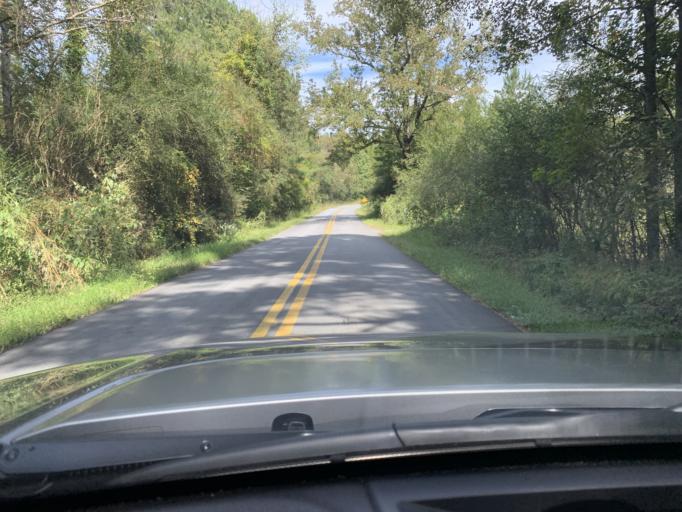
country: US
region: Georgia
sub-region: Polk County
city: Cedartown
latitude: 33.9543
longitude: -85.3516
